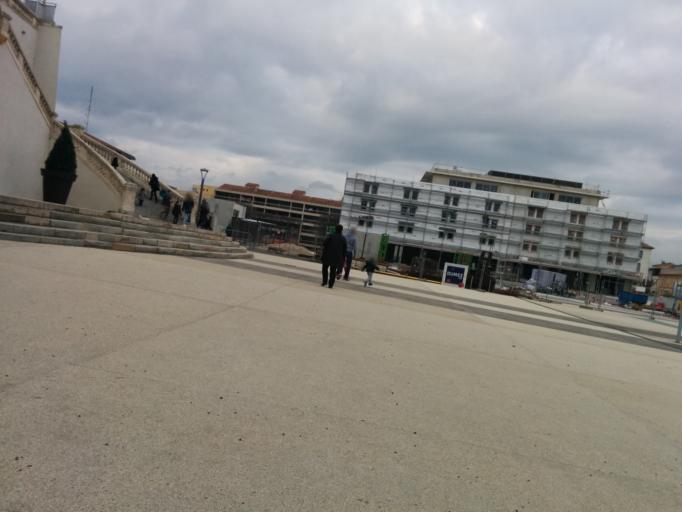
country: FR
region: Languedoc-Roussillon
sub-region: Departement du Gard
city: Ales
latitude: 44.1263
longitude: 4.0783
